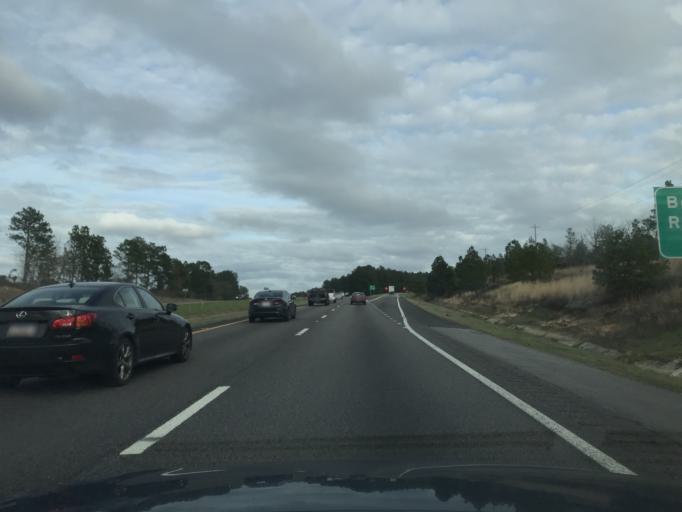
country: US
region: South Carolina
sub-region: Aiken County
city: Graniteville
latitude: 33.6041
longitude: -81.8501
